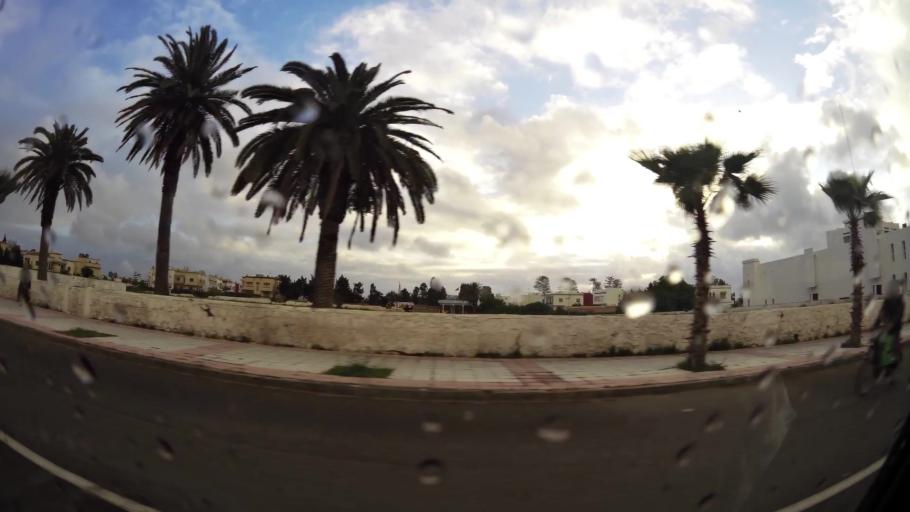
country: MA
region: Doukkala-Abda
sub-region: El-Jadida
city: El Jadida
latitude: 33.2441
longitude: -8.5052
